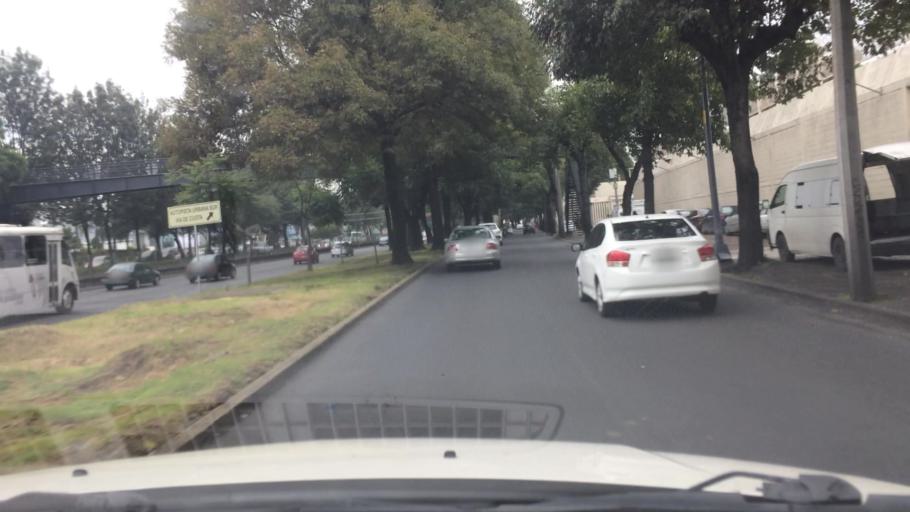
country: MX
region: Mexico City
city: Tlalpan
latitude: 19.2834
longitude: -99.1434
